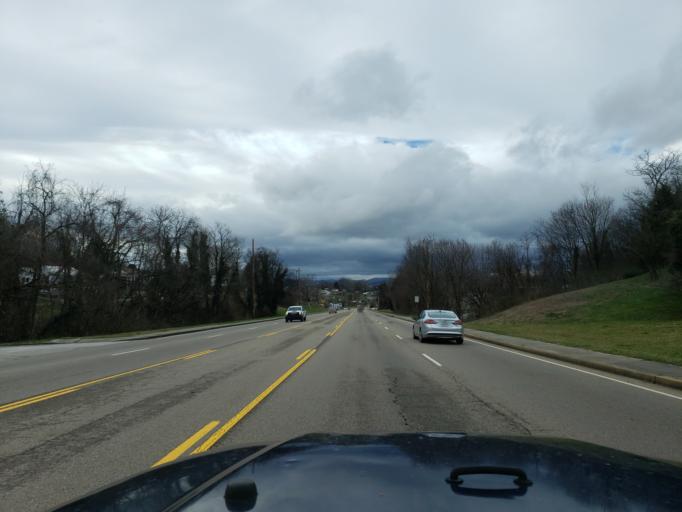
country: US
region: Tennessee
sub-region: Jefferson County
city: Jefferson City
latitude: 36.0931
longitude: -83.4760
